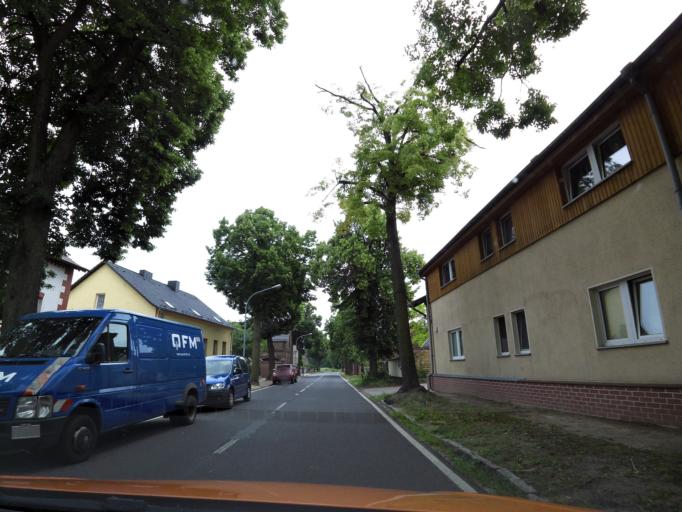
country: DE
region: Brandenburg
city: Rangsdorf
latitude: 52.2981
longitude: 13.3867
